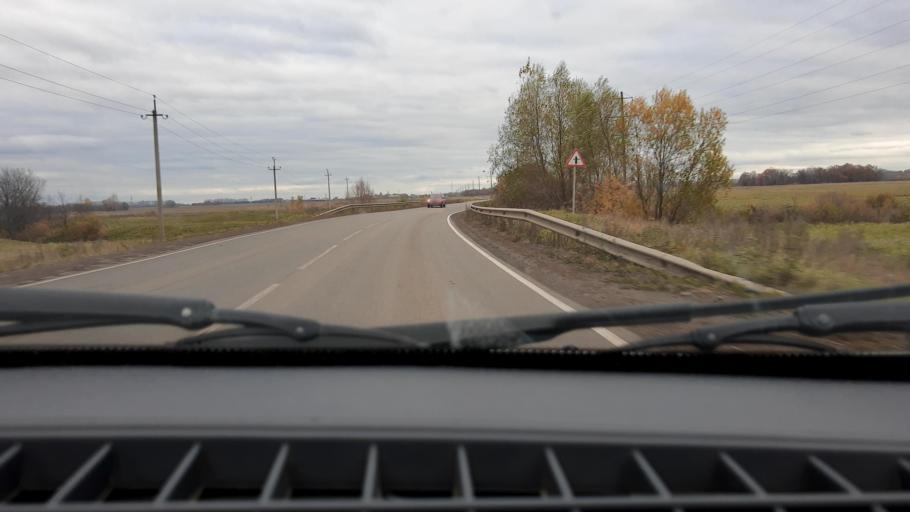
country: RU
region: Bashkortostan
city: Kabakovo
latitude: 54.5634
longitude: 55.9963
